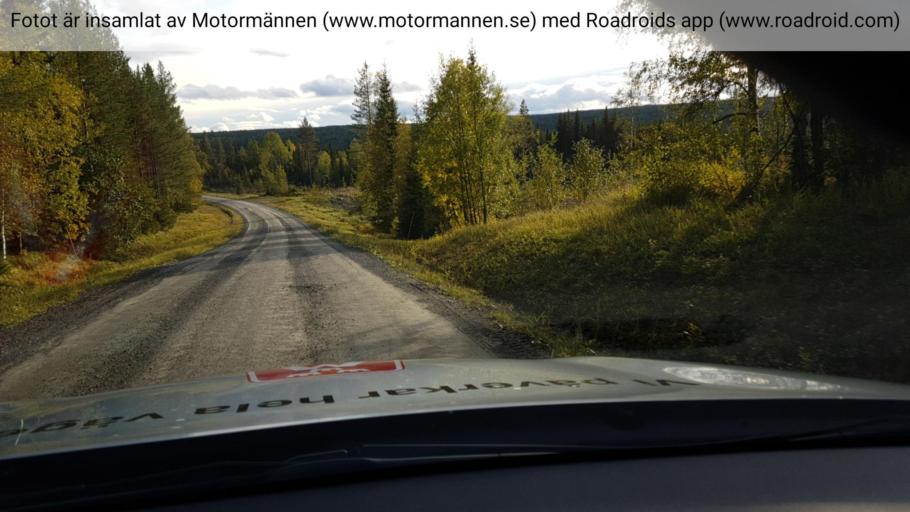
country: SE
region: Jaemtland
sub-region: Krokoms Kommun
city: Krokom
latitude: 63.6811
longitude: 14.5788
